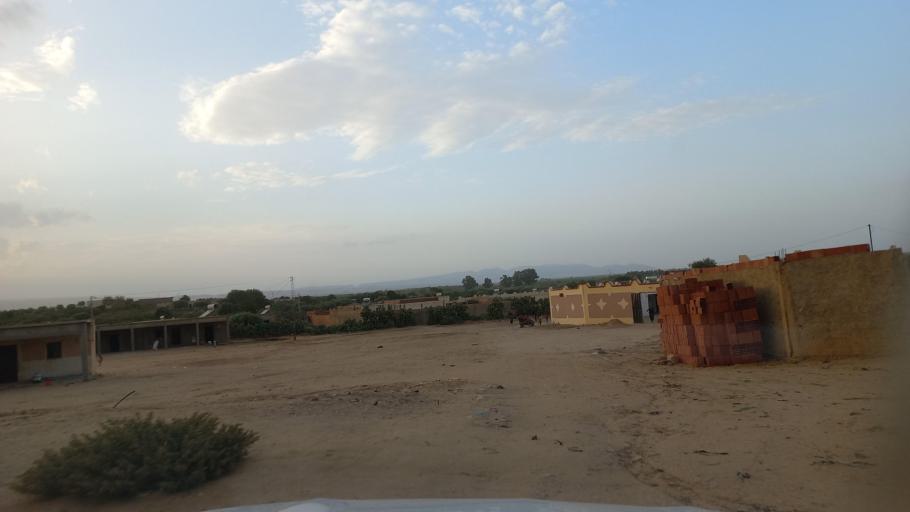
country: TN
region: Al Qasrayn
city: Kasserine
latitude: 35.2664
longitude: 9.0574
